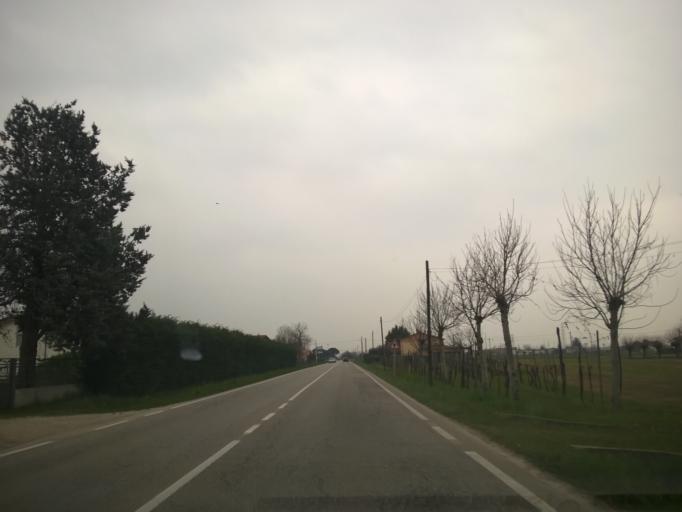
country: IT
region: Veneto
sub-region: Provincia di Vicenza
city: Montecchio Precalcino
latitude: 45.6841
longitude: 11.5662
